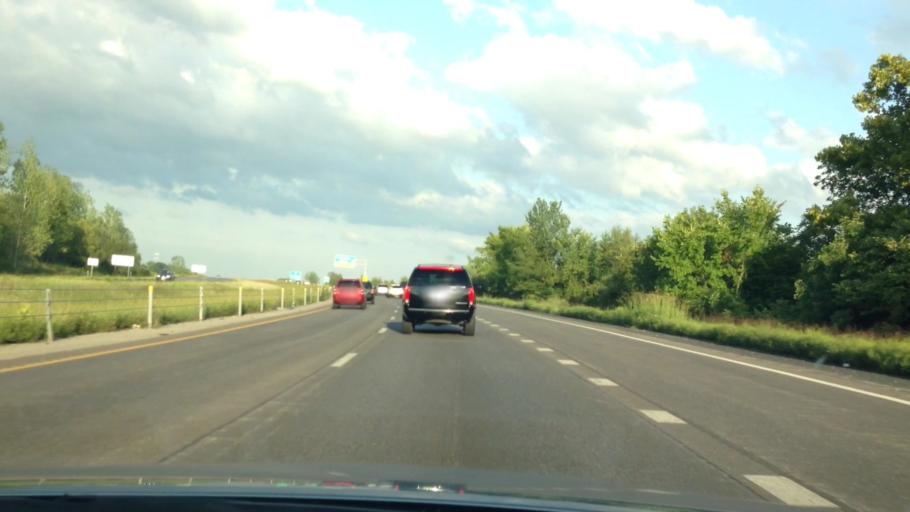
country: US
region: Missouri
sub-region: Clay County
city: Gladstone
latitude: 39.2422
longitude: -94.5274
